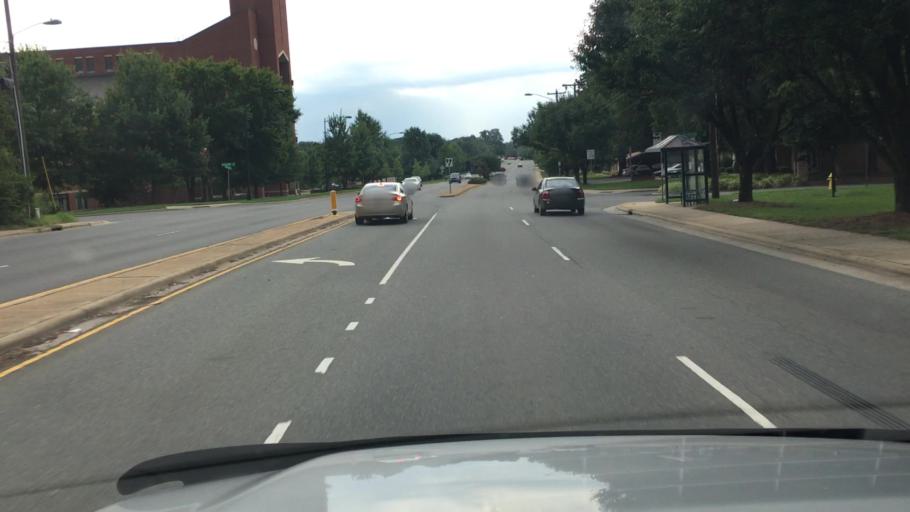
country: US
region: North Carolina
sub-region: Mecklenburg County
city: Charlotte
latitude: 35.2811
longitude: -80.8567
